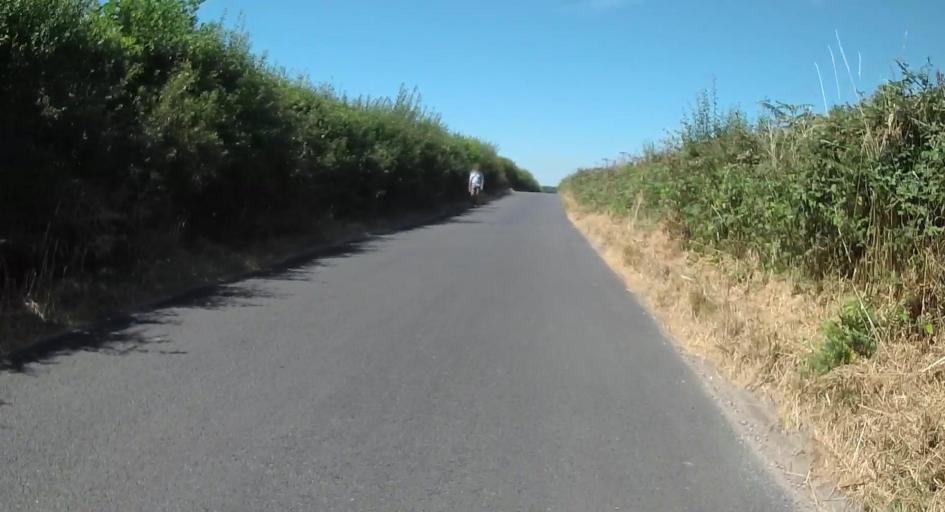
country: GB
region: England
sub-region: Dorset
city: Wool
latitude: 50.6329
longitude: -2.1932
